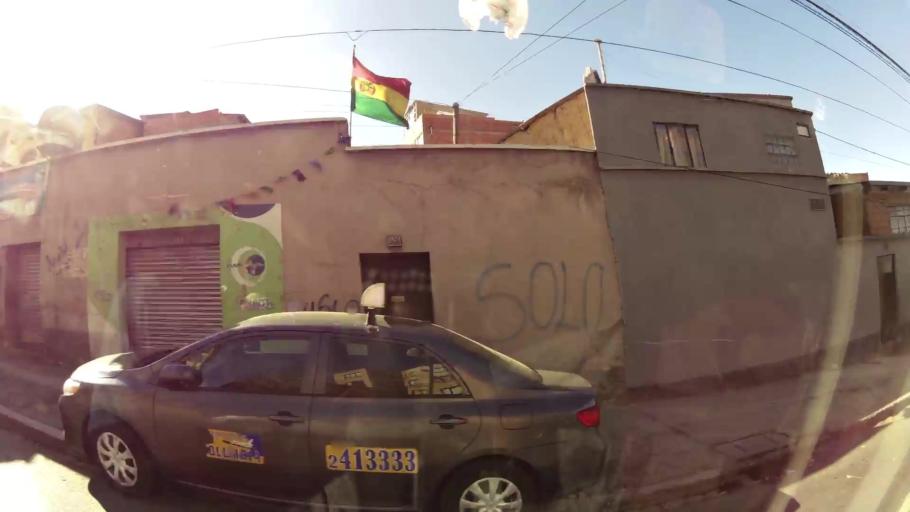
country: BO
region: La Paz
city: La Paz
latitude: -16.5156
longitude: -68.1333
